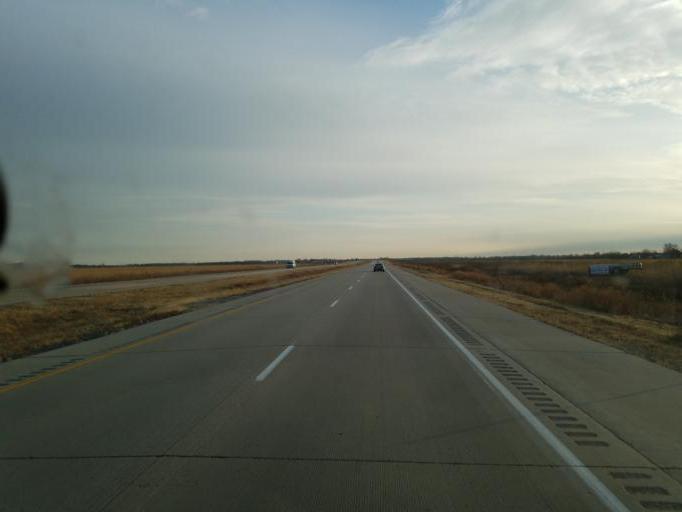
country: US
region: Nebraska
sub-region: Burt County
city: Tekamah
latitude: 41.8729
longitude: -96.1039
